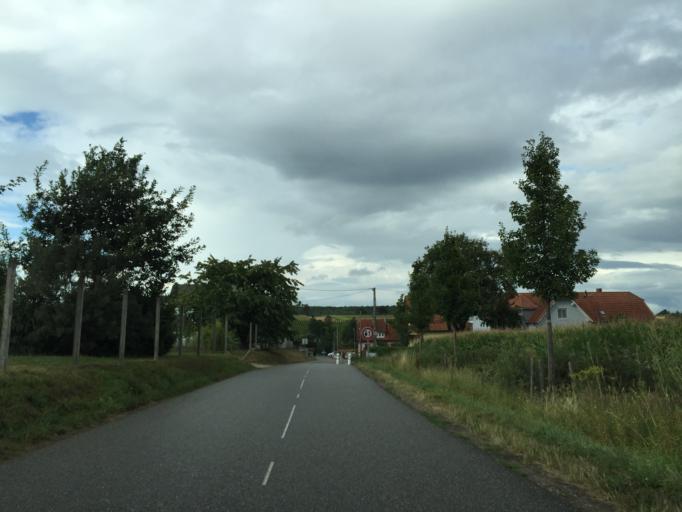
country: FR
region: Alsace
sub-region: Departement du Bas-Rhin
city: Soultz-sous-Forets
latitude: 48.9838
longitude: 7.9015
